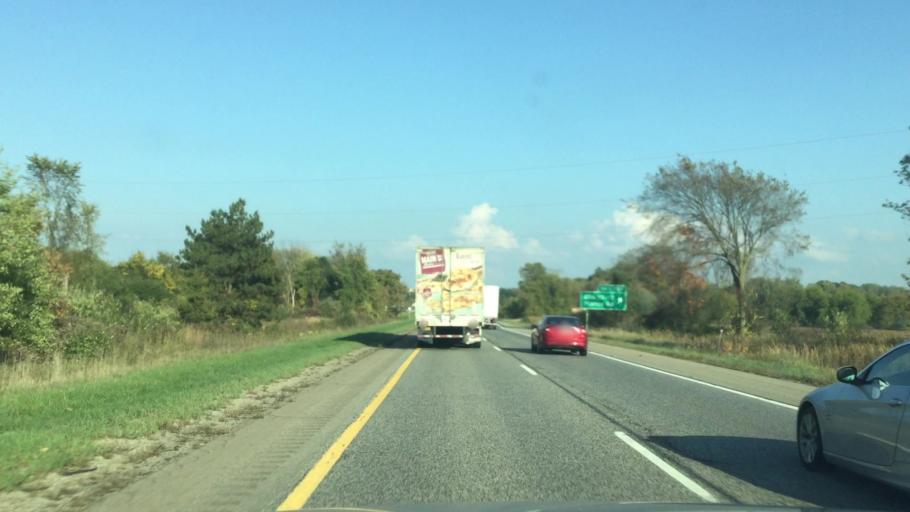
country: US
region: Michigan
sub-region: Washtenaw County
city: Chelsea
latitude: 42.2915
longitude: -84.0800
